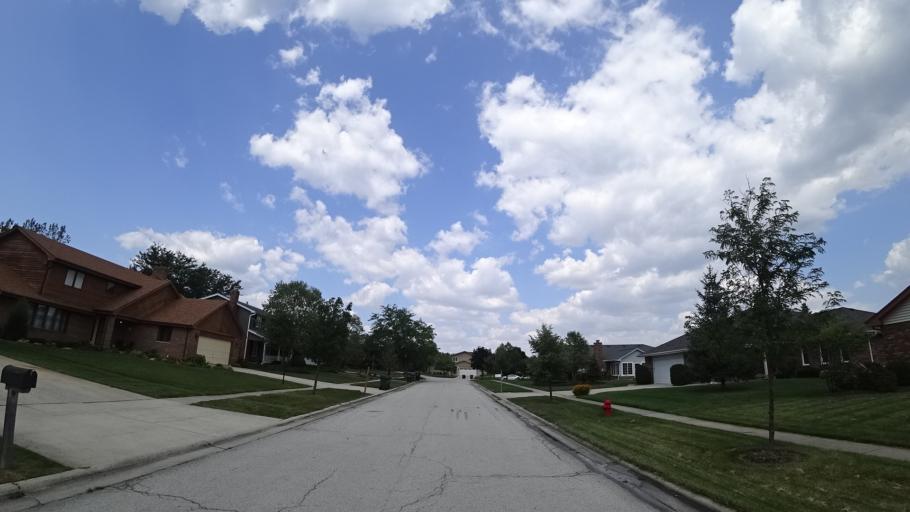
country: US
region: Illinois
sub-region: Cook County
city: Oak Forest
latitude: 41.6223
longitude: -87.7756
